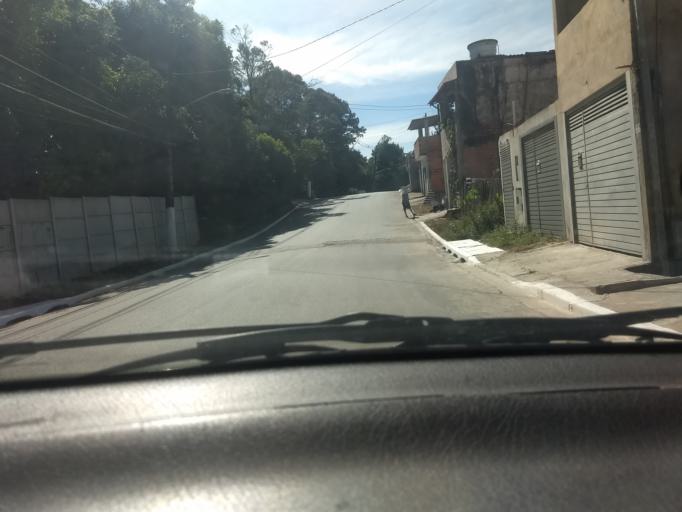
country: BR
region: Sao Paulo
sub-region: Embu-Guacu
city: Embu Guacu
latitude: -23.8226
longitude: -46.7067
